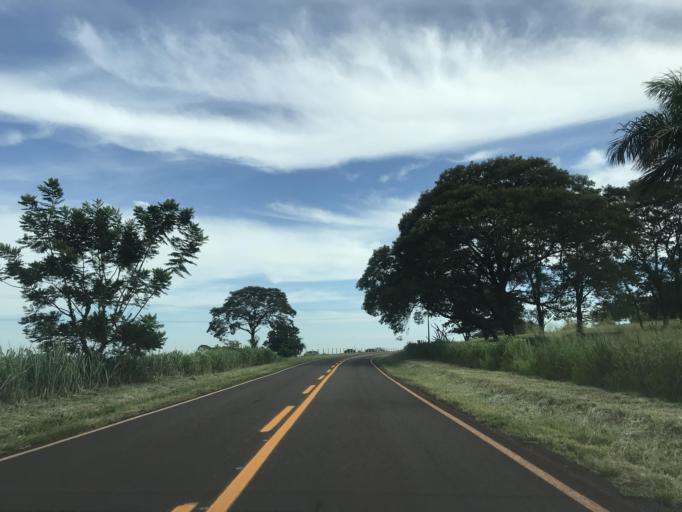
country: BR
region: Parana
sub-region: Terra Rica
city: Terra Rica
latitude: -22.7836
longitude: -52.6569
